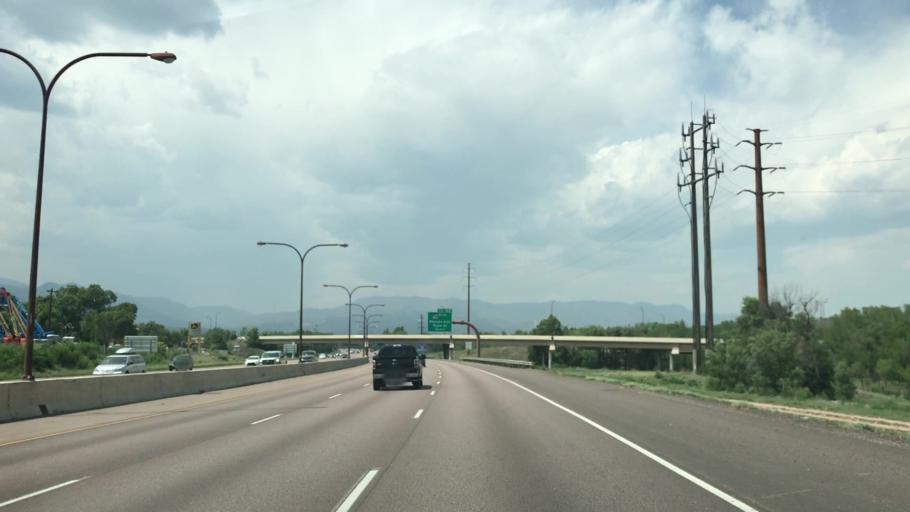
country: US
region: Colorado
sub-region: El Paso County
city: Colorado Springs
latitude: 38.8062
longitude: -104.8036
